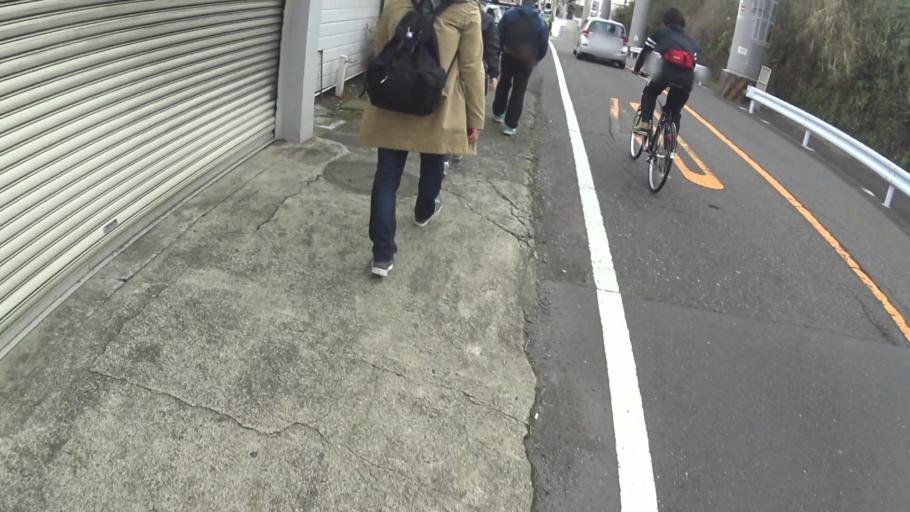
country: JP
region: Kanagawa
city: Fujisawa
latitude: 35.3211
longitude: 139.5055
